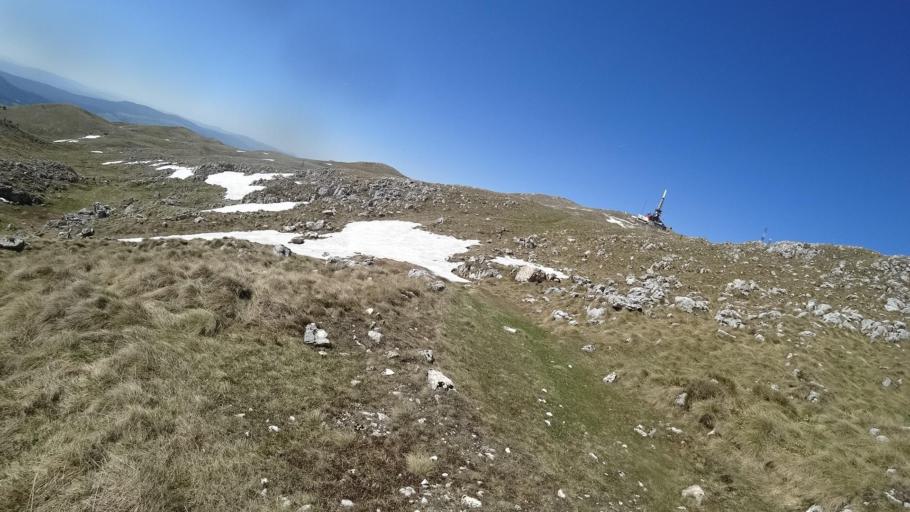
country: BA
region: Federation of Bosnia and Herzegovina
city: Travnik
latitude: 44.2866
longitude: 17.6349
